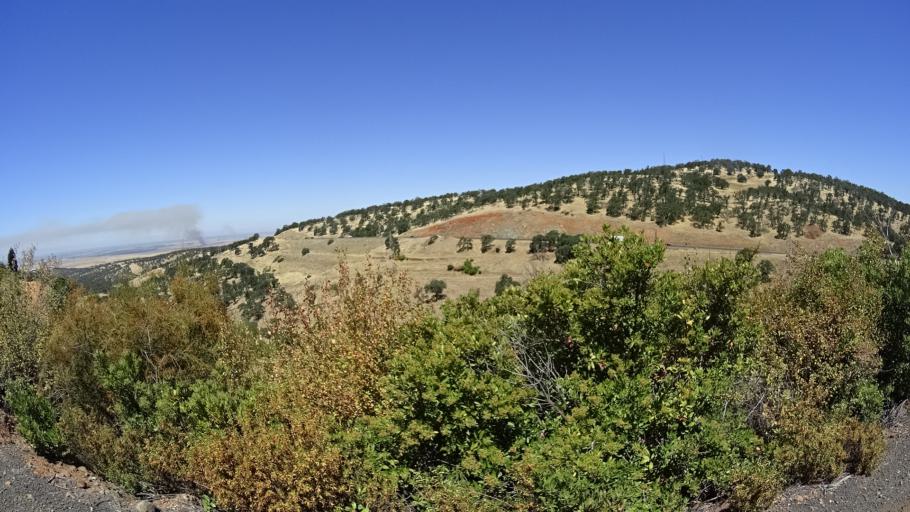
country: US
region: California
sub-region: Calaveras County
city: Copperopolis
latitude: 37.9416
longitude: -120.7011
